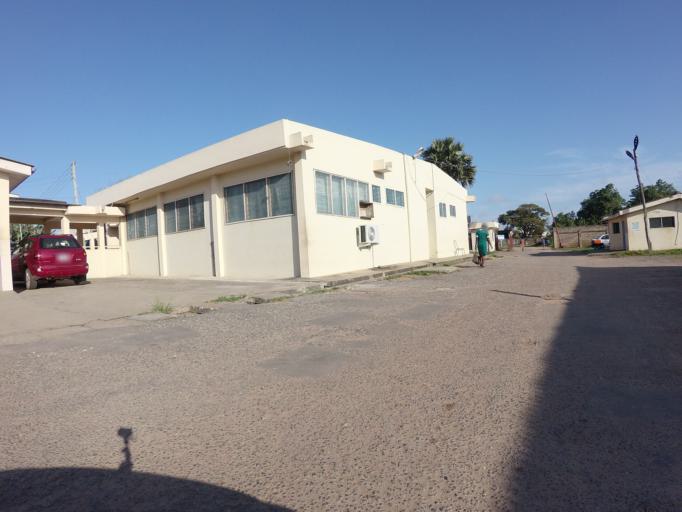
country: GH
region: Greater Accra
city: Accra
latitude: 5.5377
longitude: -0.2232
